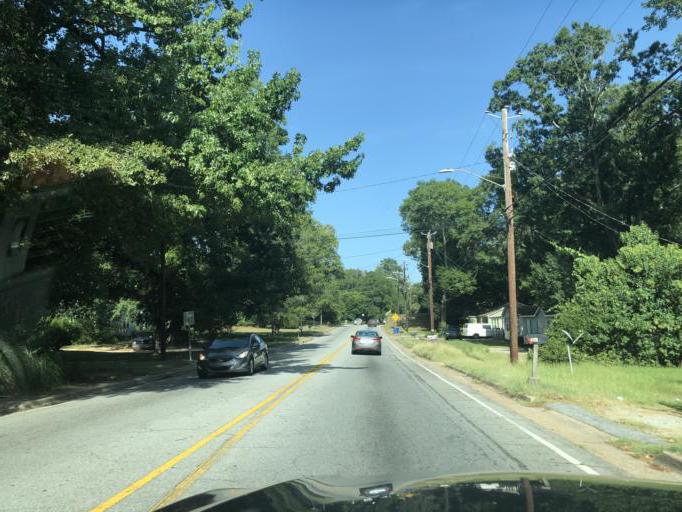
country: US
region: Georgia
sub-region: Muscogee County
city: Columbus
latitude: 32.4842
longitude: -84.9207
